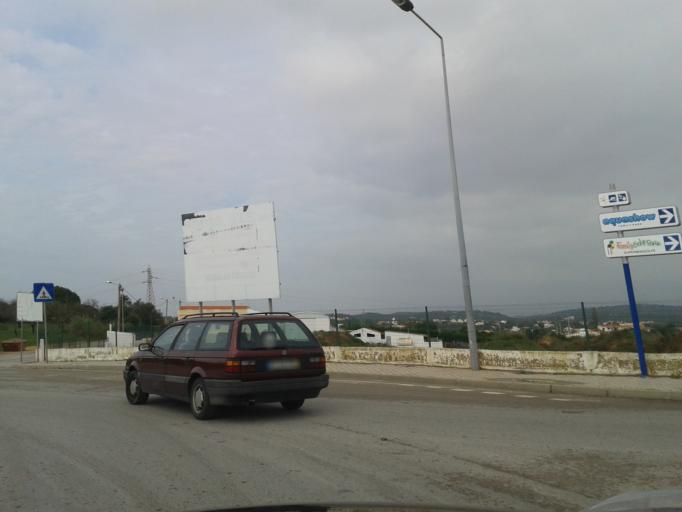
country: PT
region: Faro
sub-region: Loule
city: Boliqueime
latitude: 37.1059
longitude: -8.1869
